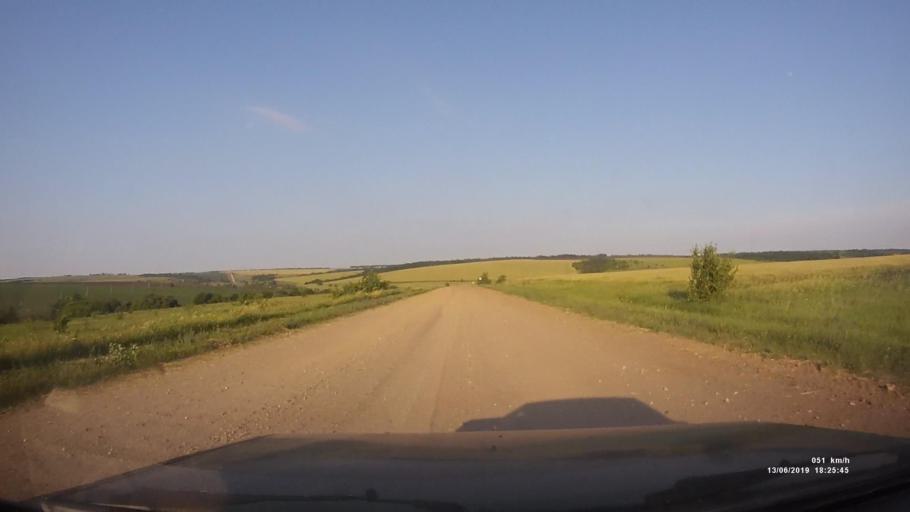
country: RU
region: Rostov
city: Kazanskaya
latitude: 49.8512
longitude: 41.3076
